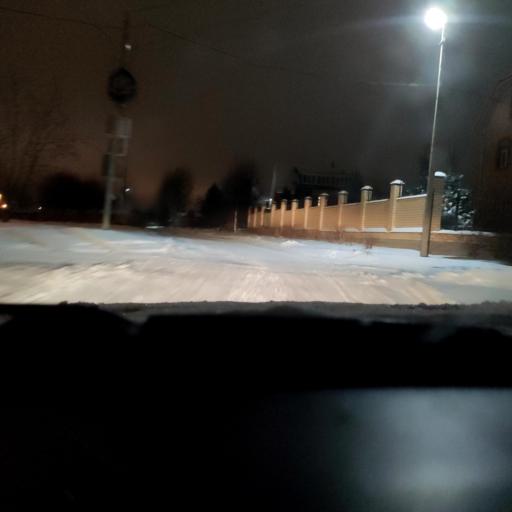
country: RU
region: Perm
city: Ferma
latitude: 57.9107
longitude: 56.3125
